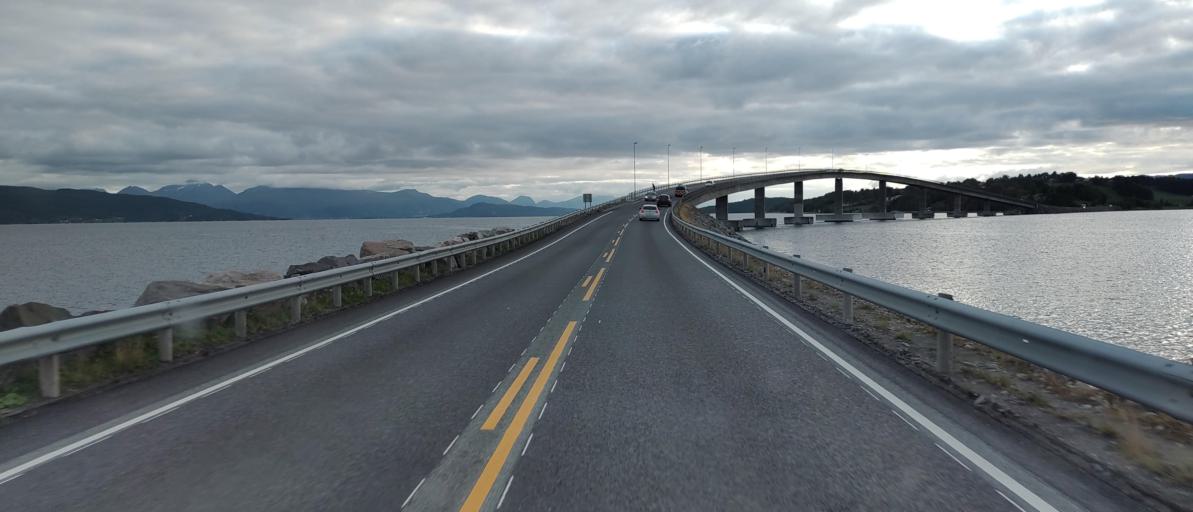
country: NO
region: More og Romsdal
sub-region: Molde
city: Hjelset
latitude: 62.7312
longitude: 7.3633
